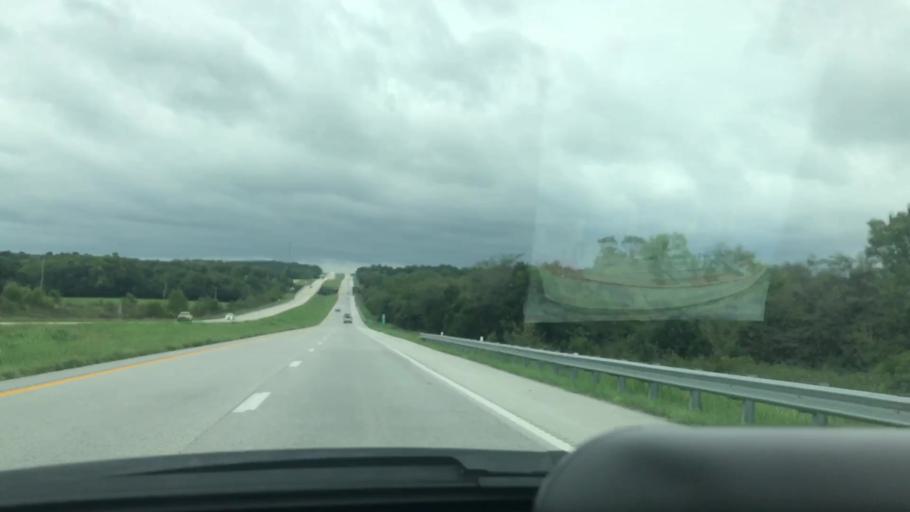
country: US
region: Missouri
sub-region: Greene County
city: Fair Grove
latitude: 37.4105
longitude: -93.1456
